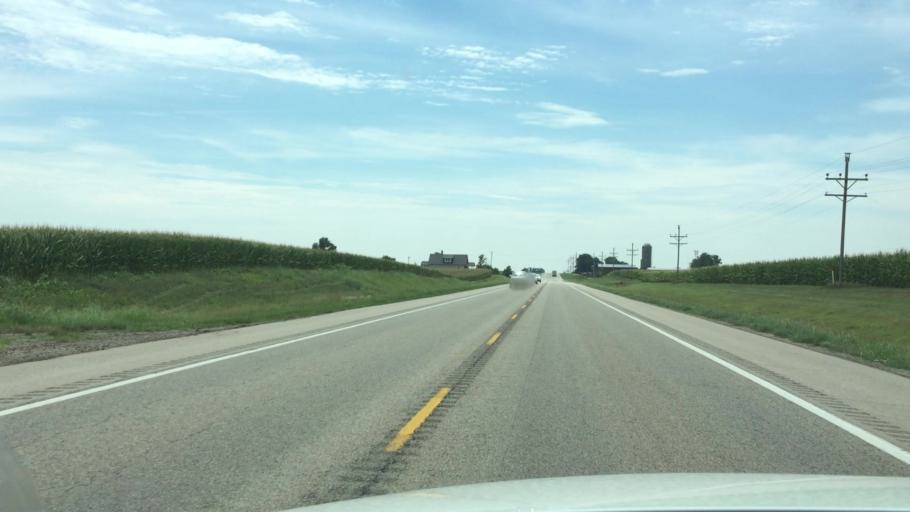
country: US
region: Kansas
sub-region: Nemaha County
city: Sabetha
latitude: 39.7796
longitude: -95.7295
